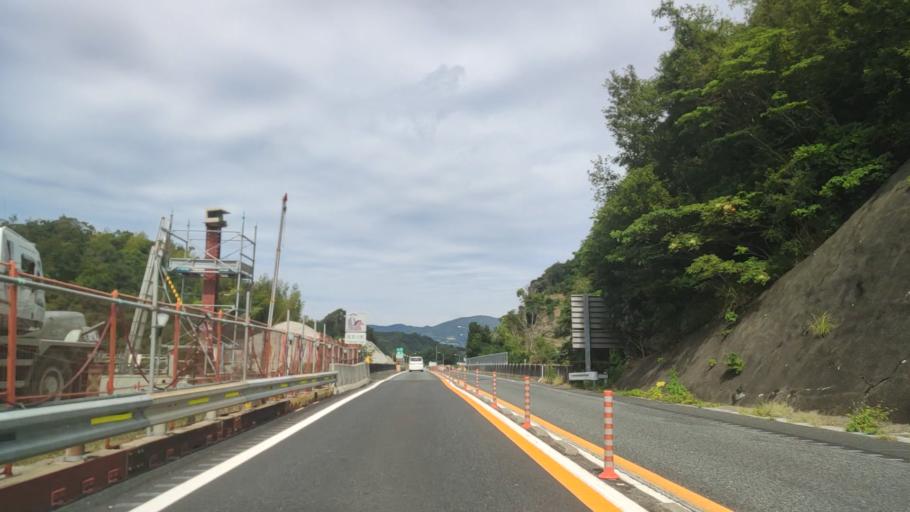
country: JP
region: Wakayama
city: Kainan
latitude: 34.0334
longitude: 135.2009
